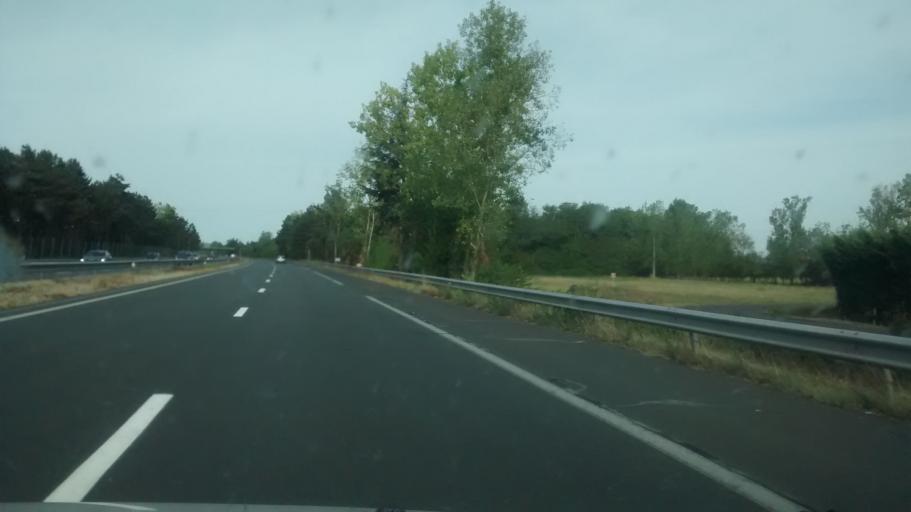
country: FR
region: Aquitaine
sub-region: Departement du Lot-et-Garonne
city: Roquefort
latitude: 44.1834
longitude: 0.5574
